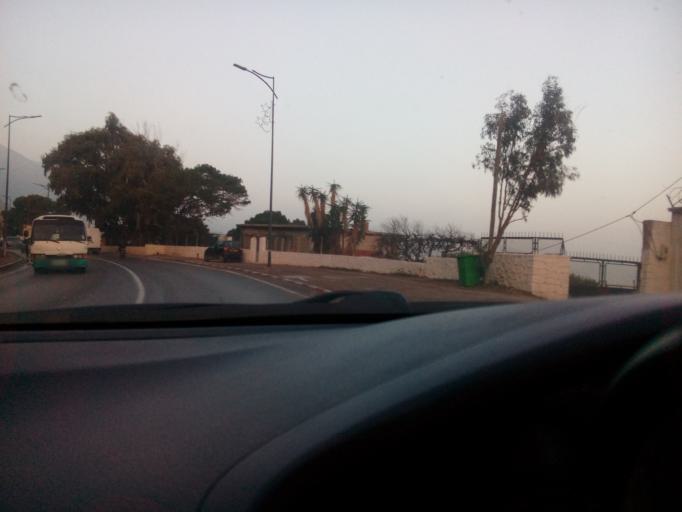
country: DZ
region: Oran
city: Oran
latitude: 35.7138
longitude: -0.6665
